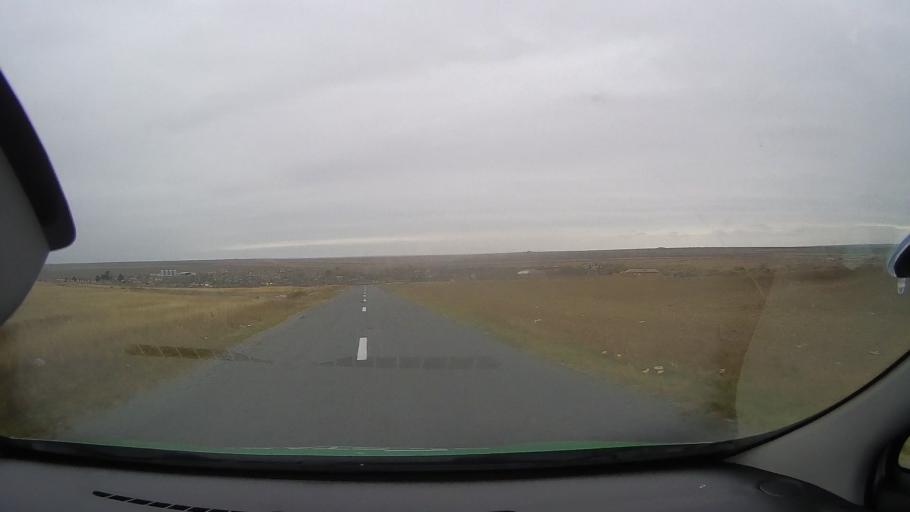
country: RO
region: Constanta
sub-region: Comuna Pantelimon
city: Pantelimon
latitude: 44.5938
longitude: 28.3234
